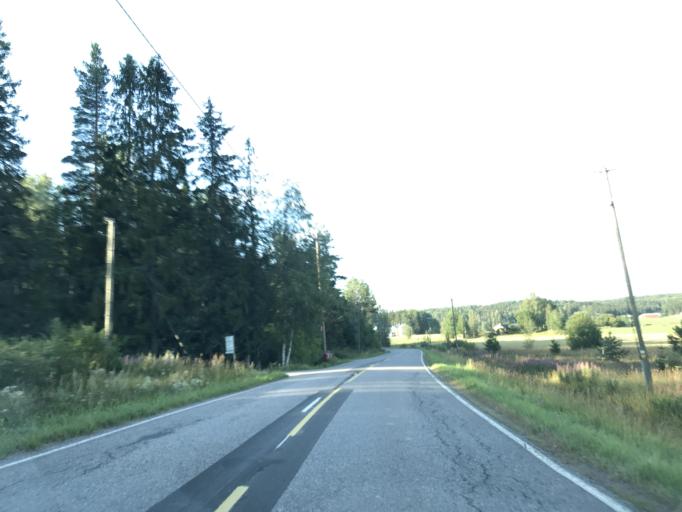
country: FI
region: Uusimaa
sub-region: Helsinki
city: Nurmijaervi
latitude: 60.3664
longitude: 24.6828
